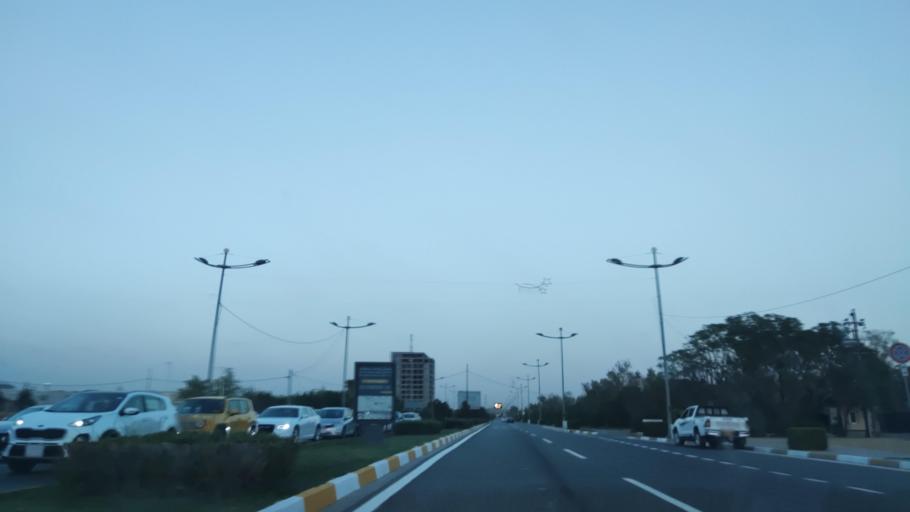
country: IQ
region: Arbil
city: Erbil
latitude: 36.1998
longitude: 43.9805
